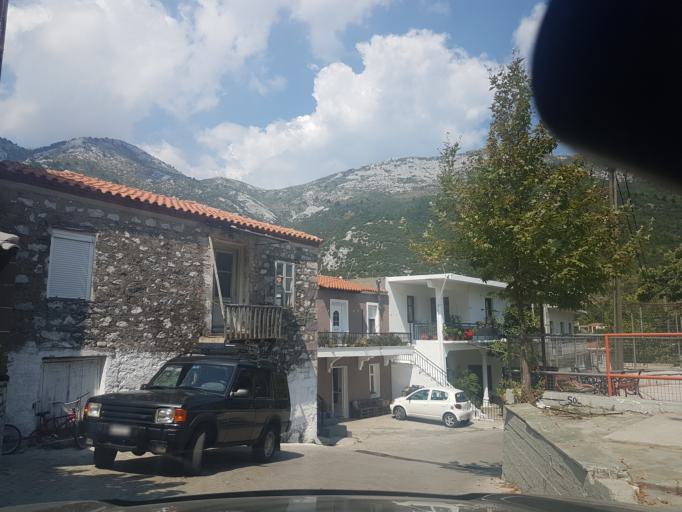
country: GR
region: Central Greece
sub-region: Nomos Evvoias
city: Yimnon
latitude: 38.6182
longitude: 23.8899
